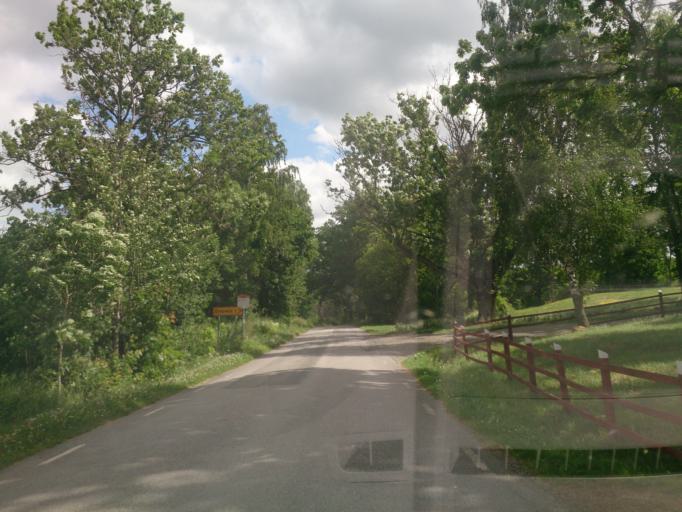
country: SE
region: OEstergoetland
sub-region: Norrkopings Kommun
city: Krokek
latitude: 58.4987
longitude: 16.5726
